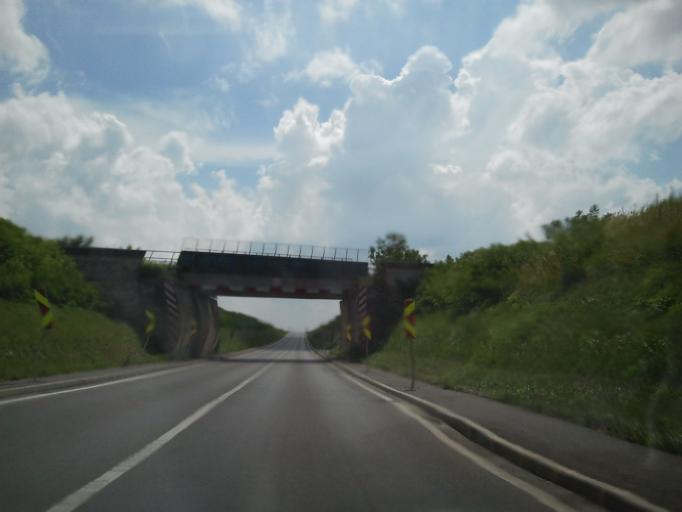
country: HR
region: Osjecko-Baranjska
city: Sarvas
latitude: 45.5297
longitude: 18.8024
